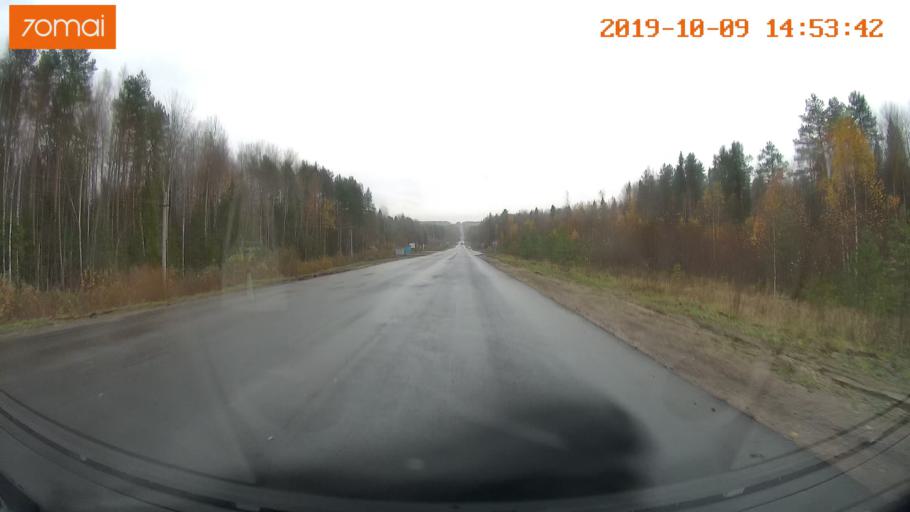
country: RU
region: Kostroma
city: Chistyye Bory
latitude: 58.3645
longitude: 41.6396
